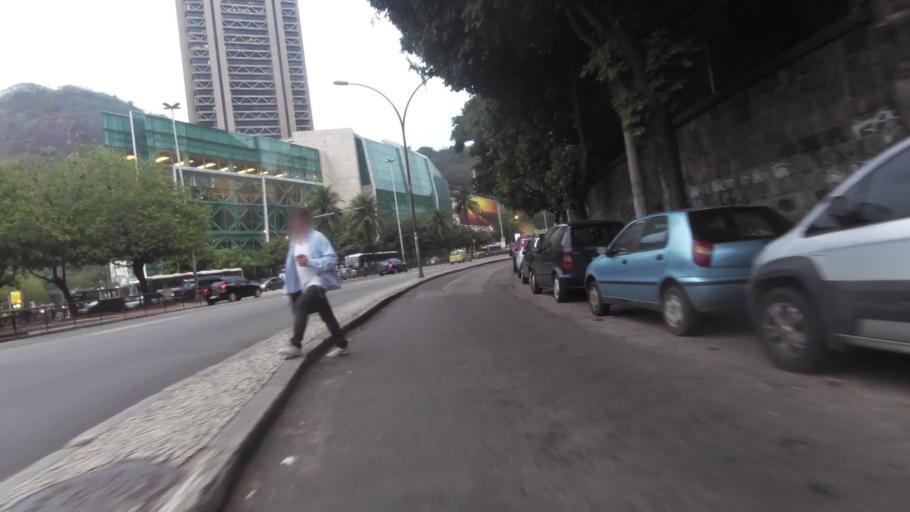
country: BR
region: Rio de Janeiro
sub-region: Rio De Janeiro
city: Rio de Janeiro
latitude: -22.9559
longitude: -43.1781
